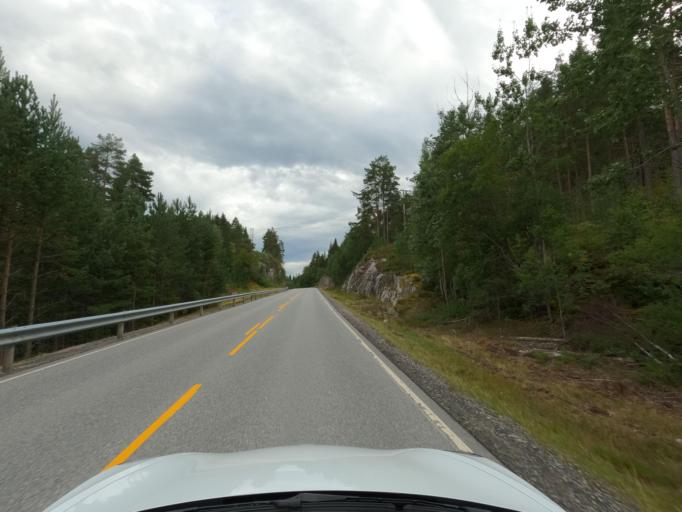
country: NO
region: Telemark
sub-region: Hjartdal
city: Sauland
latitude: 59.7429
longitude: 9.0203
